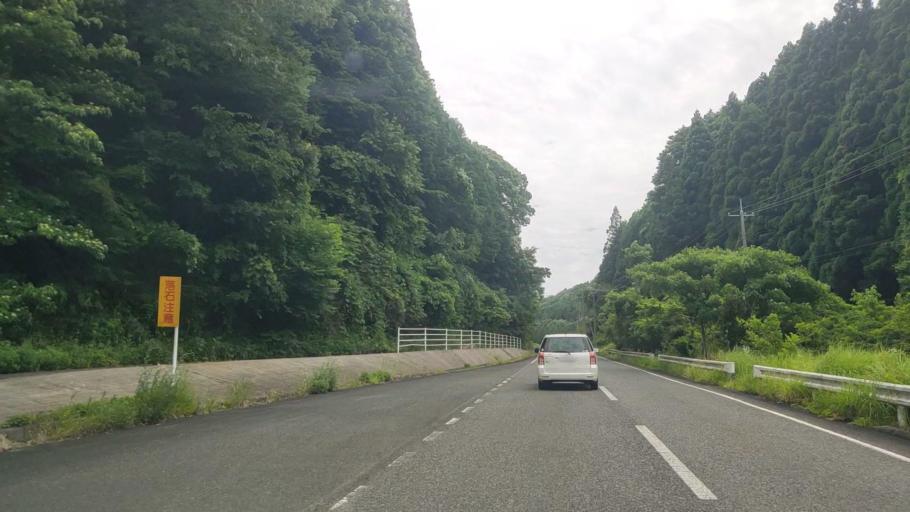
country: JP
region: Hyogo
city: Yamazakicho-nakabirose
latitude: 35.1046
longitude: 134.3061
